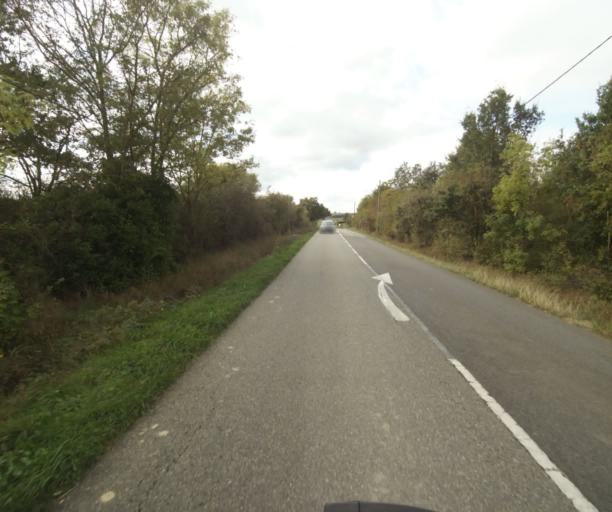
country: FR
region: Midi-Pyrenees
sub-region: Departement du Tarn-et-Garonne
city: Verdun-sur-Garonne
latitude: 43.8506
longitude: 1.1408
